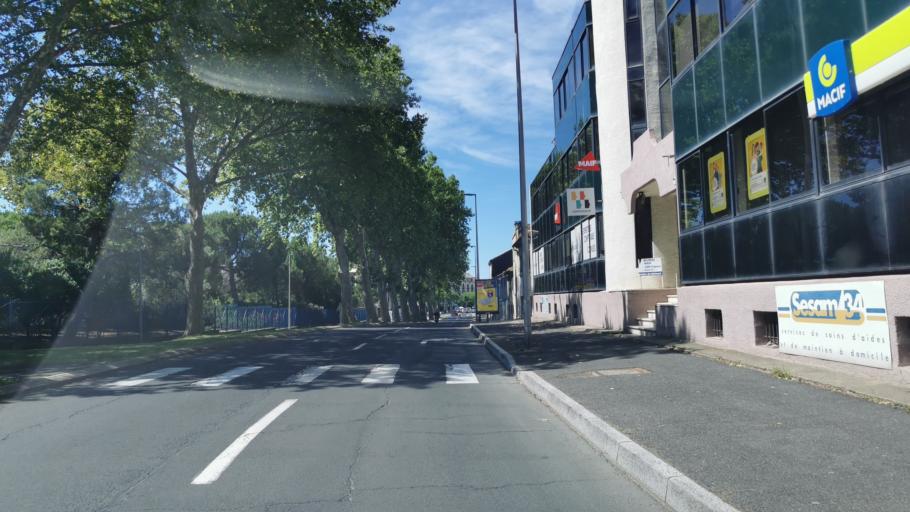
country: FR
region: Languedoc-Roussillon
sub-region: Departement de l'Herault
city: Beziers
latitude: 43.3525
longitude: 3.2243
